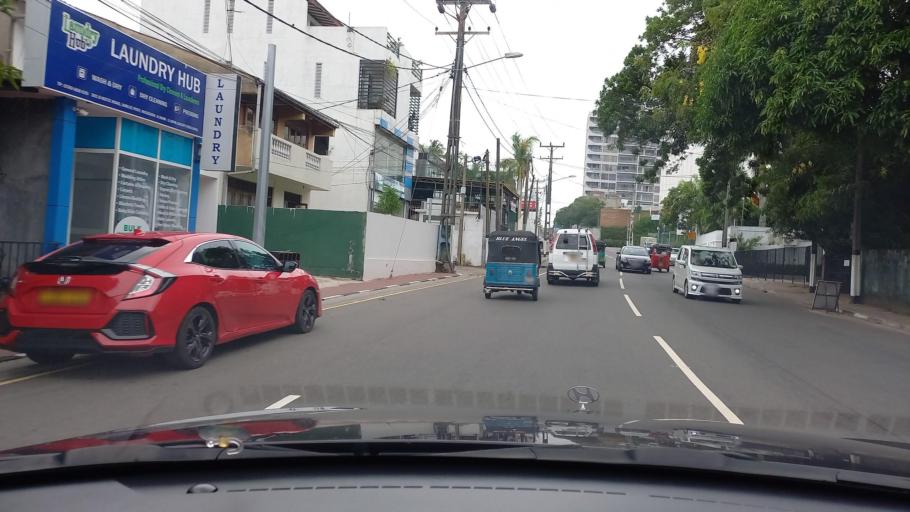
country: LK
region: Western
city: Sri Jayewardenepura Kotte
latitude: 6.8771
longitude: 79.9004
